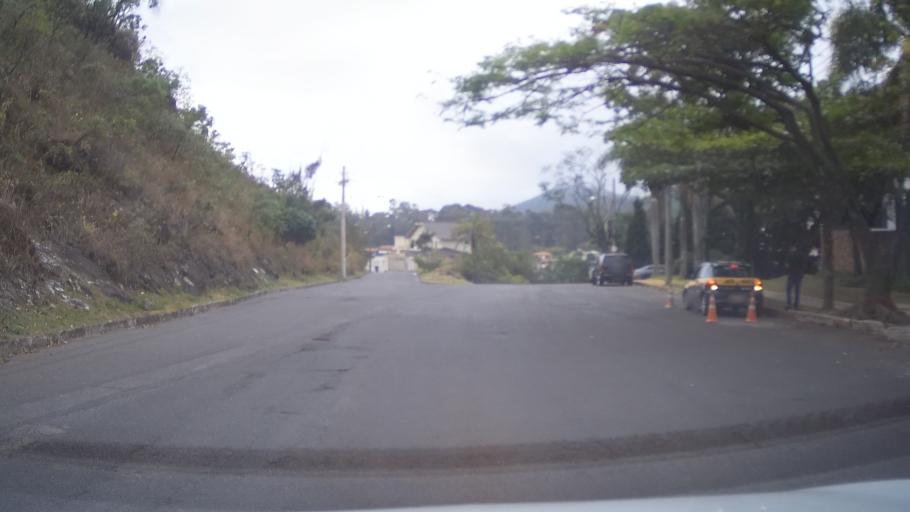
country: BR
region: Minas Gerais
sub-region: Belo Horizonte
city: Belo Horizonte
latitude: -19.9588
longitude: -43.9175
